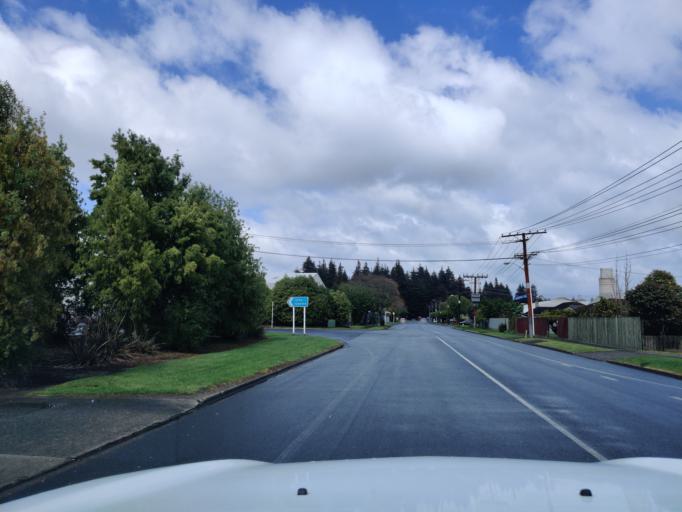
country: NZ
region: Bay of Plenty
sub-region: Rotorua District
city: Rotorua
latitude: -38.1463
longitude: 176.2752
